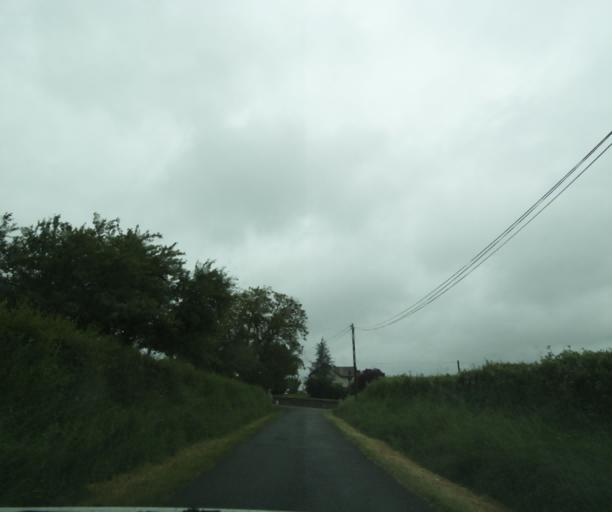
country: FR
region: Bourgogne
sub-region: Departement de Saone-et-Loire
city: Palinges
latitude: 46.4941
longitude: 4.2150
